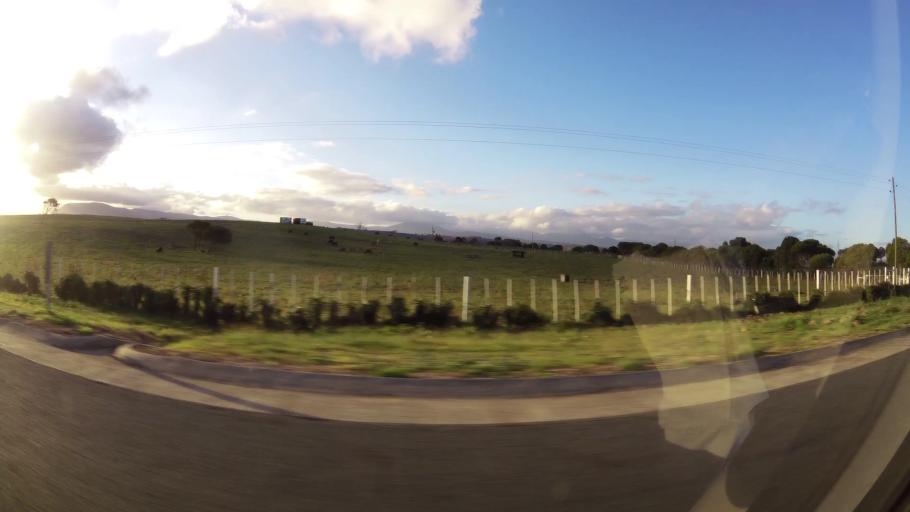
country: ZA
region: Western Cape
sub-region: Eden District Municipality
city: George
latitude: -34.0029
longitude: 22.7035
